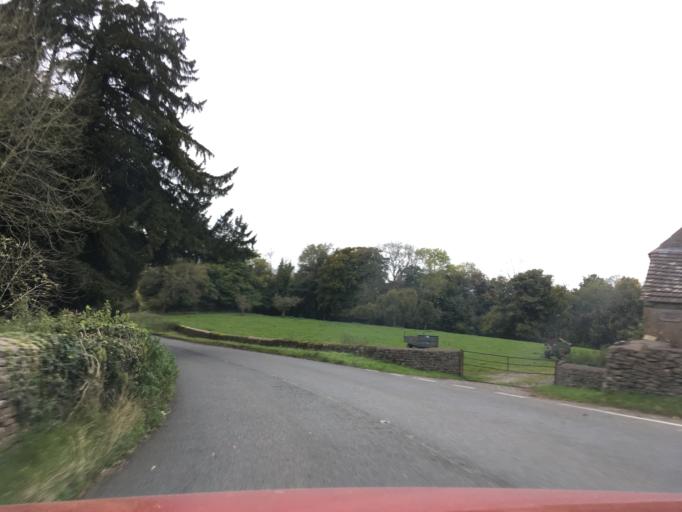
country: GB
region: England
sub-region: Gloucestershire
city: Dursley
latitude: 51.6687
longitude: -2.3124
